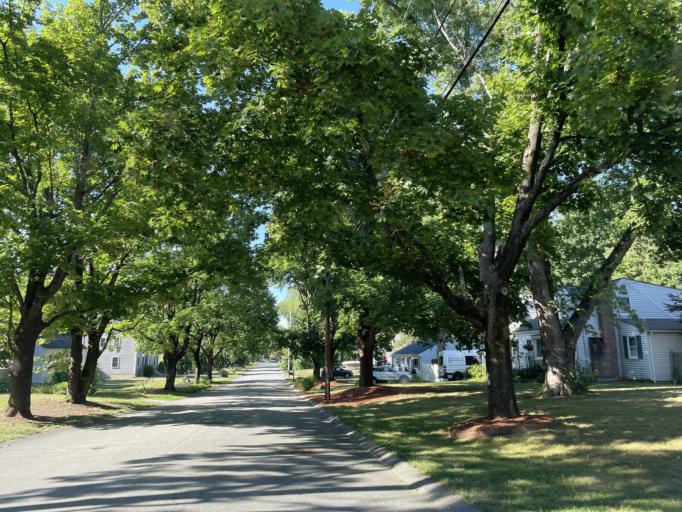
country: US
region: Massachusetts
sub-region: Norfolk County
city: Bellingham
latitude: 42.0940
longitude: -71.4361
